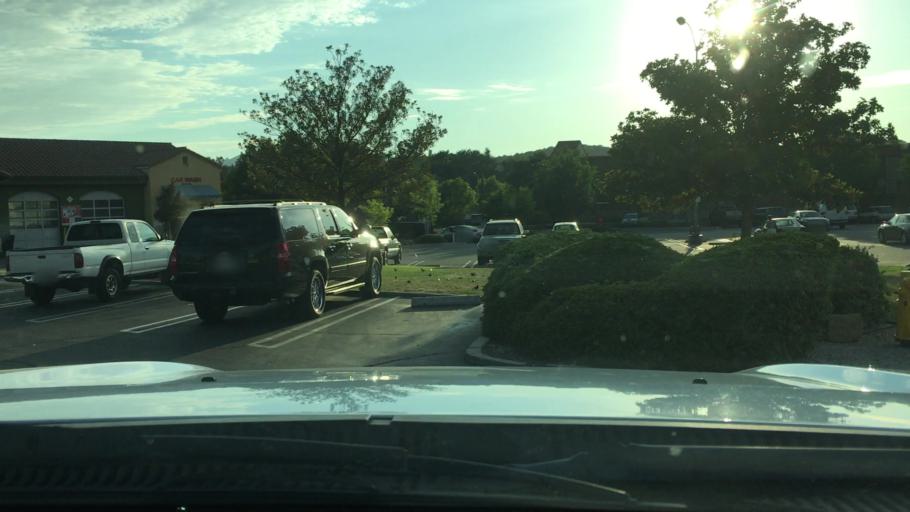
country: US
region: California
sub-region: San Luis Obispo County
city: Atascadero
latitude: 35.4872
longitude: -120.6624
